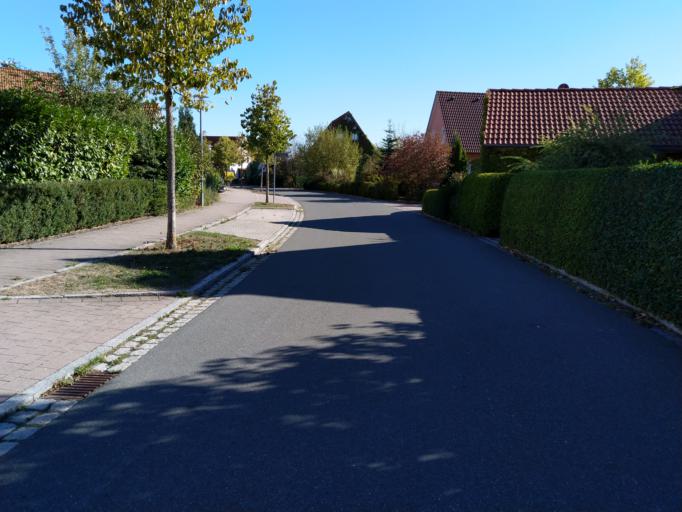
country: DE
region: Bavaria
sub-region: Regierungsbezirk Mittelfranken
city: Hagenbuchach
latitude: 49.5364
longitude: 10.7630
